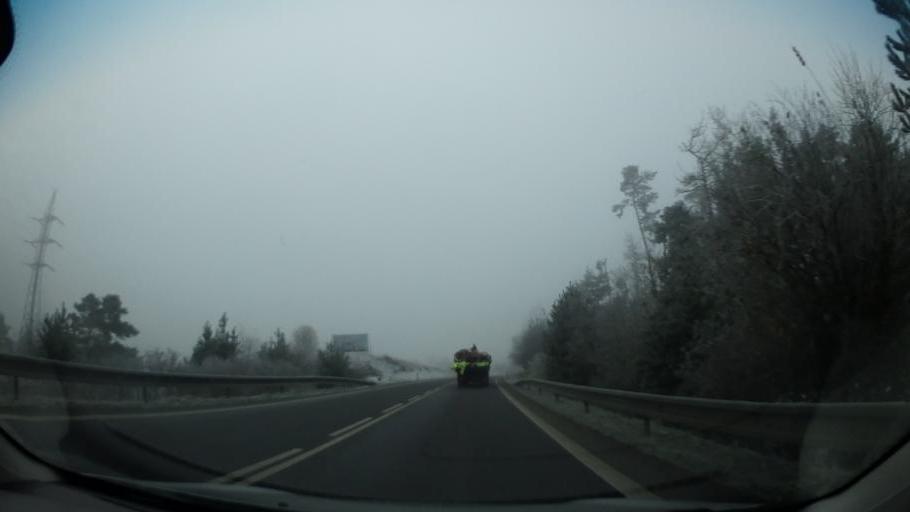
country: CZ
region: Vysocina
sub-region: Okres Trebic
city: Trebic
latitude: 49.2503
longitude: 15.9086
